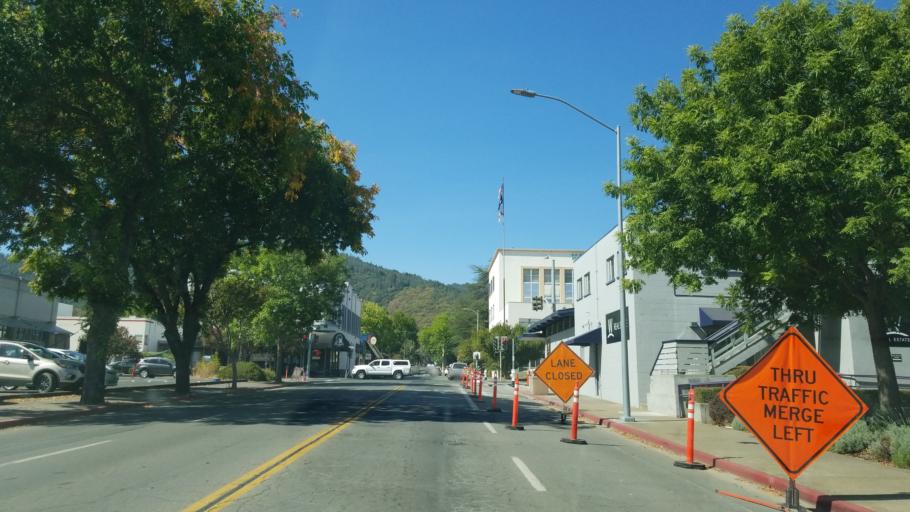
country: US
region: California
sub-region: Mendocino County
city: Ukiah
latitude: 39.1502
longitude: -123.2069
